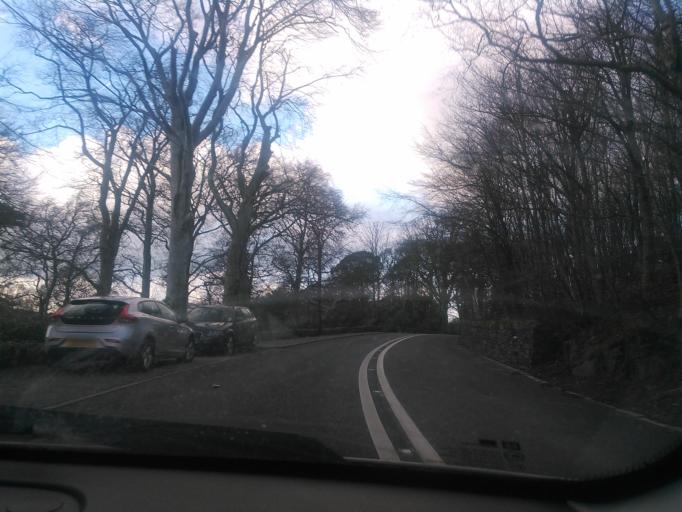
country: GB
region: Wales
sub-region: Gwynedd
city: Bethesda
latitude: 53.1682
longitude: -4.0551
